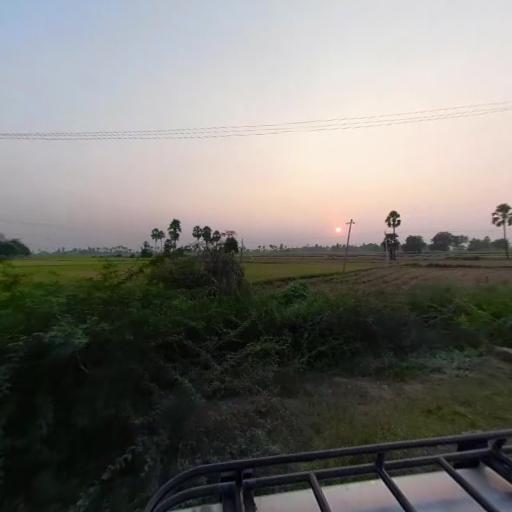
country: IN
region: Telangana
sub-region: Nalgonda
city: Suriapet
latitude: 17.0692
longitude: 79.5485
